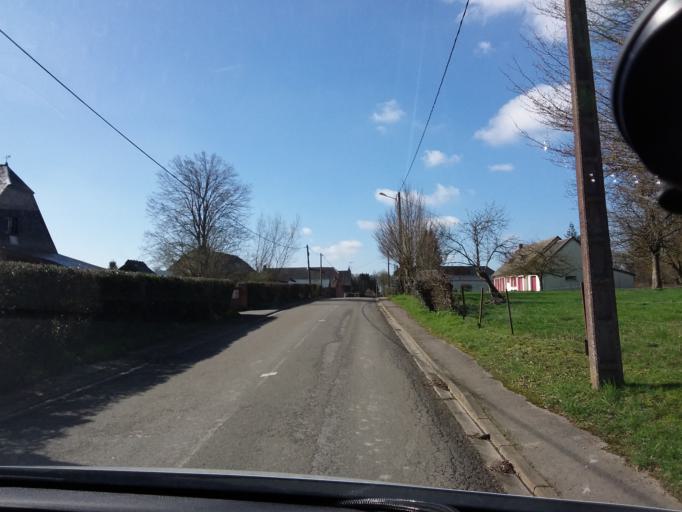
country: FR
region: Picardie
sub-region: Departement de l'Aisne
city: Hirson
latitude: 49.8536
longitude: 4.0840
